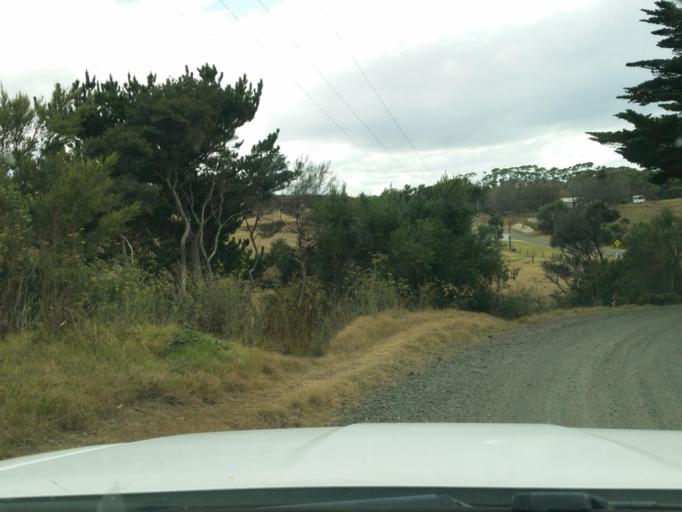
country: NZ
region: Auckland
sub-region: Auckland
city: Wellsford
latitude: -36.3610
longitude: 174.1775
